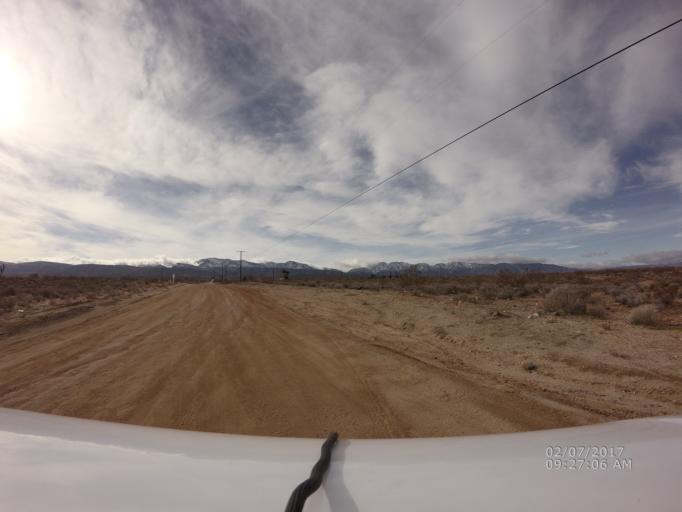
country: US
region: California
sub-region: Los Angeles County
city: Lake Los Angeles
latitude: 34.5013
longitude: -117.7653
